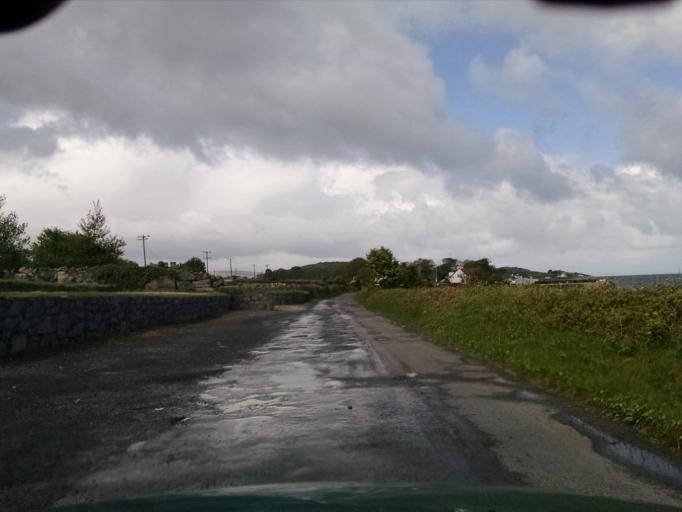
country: IE
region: Connaught
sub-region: County Galway
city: Gaillimh
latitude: 53.1557
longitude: -9.0711
